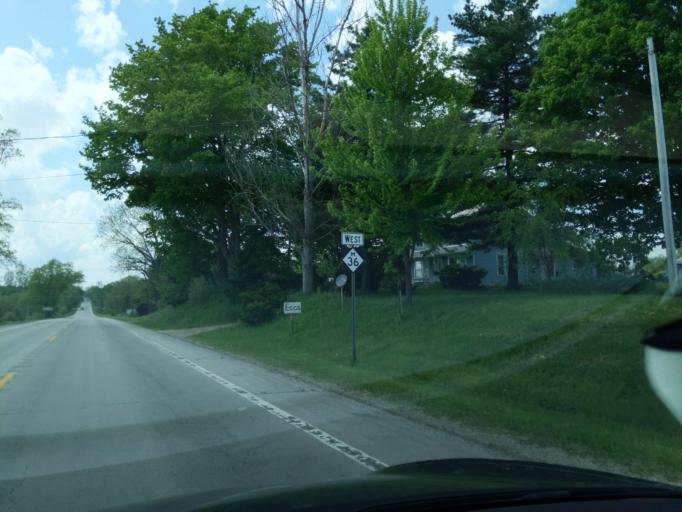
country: US
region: Michigan
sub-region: Ingham County
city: Mason
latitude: 42.5559
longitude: -84.3181
